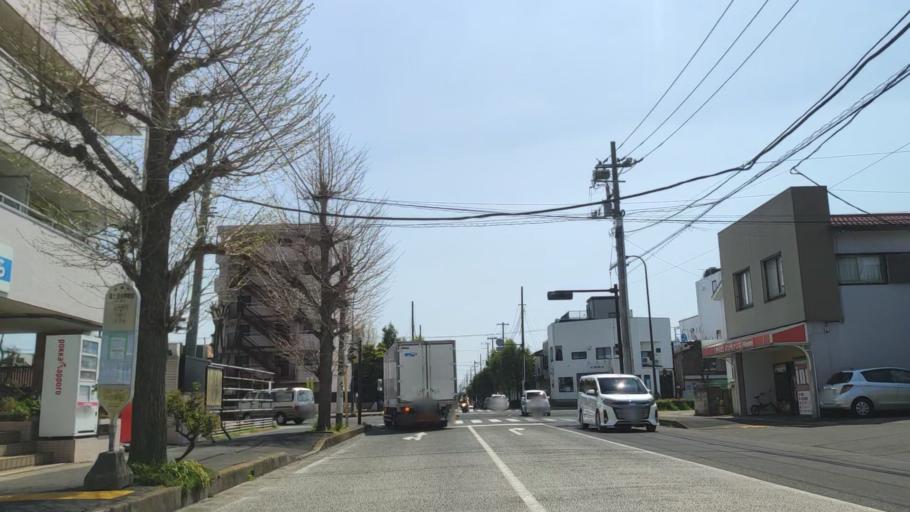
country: JP
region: Kanagawa
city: Hiratsuka
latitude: 35.3314
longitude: 139.3360
